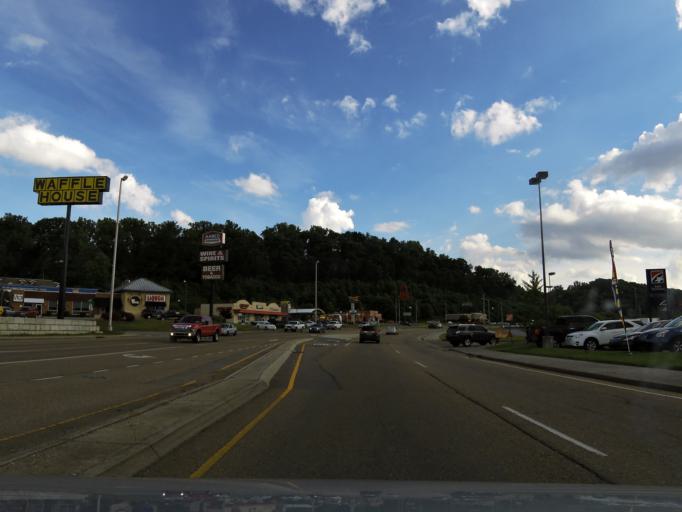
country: US
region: Tennessee
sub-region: Knox County
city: Knoxville
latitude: 36.0062
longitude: -84.0198
